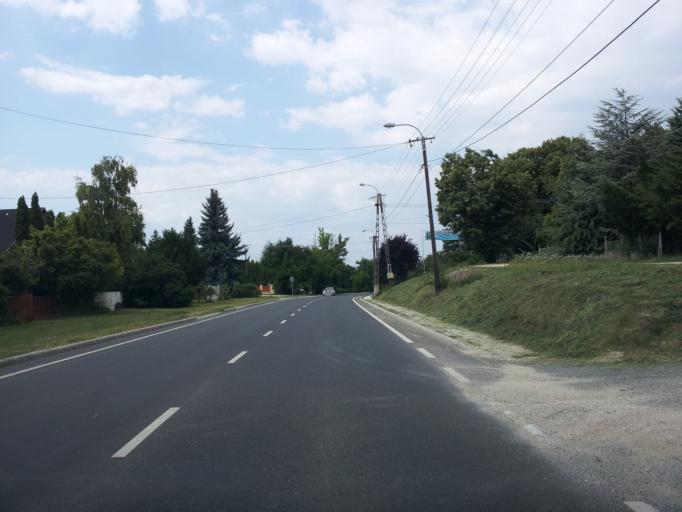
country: HU
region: Veszprem
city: Balatonkenese
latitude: 47.0234
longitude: 18.1456
